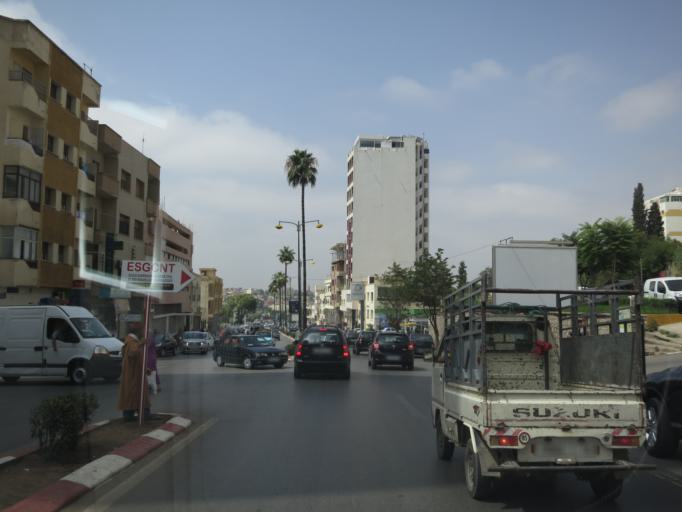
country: MA
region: Meknes-Tafilalet
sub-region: Meknes
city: Meknes
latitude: 33.8956
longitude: -5.5475
